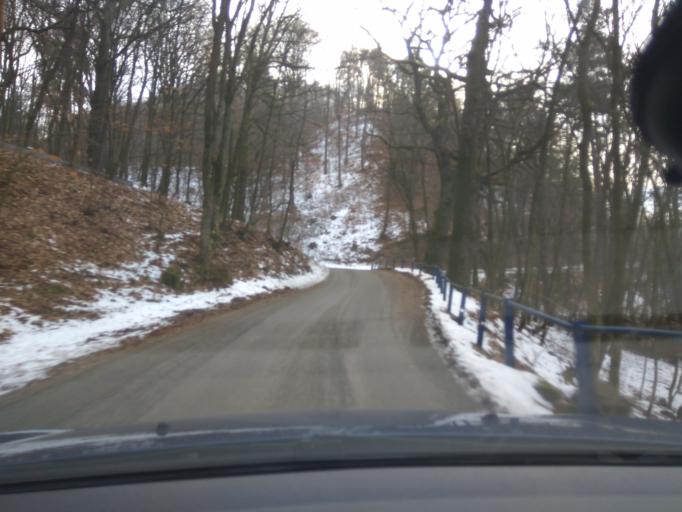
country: SK
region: Banskobystricky
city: Zarnovica
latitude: 48.4797
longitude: 18.7354
